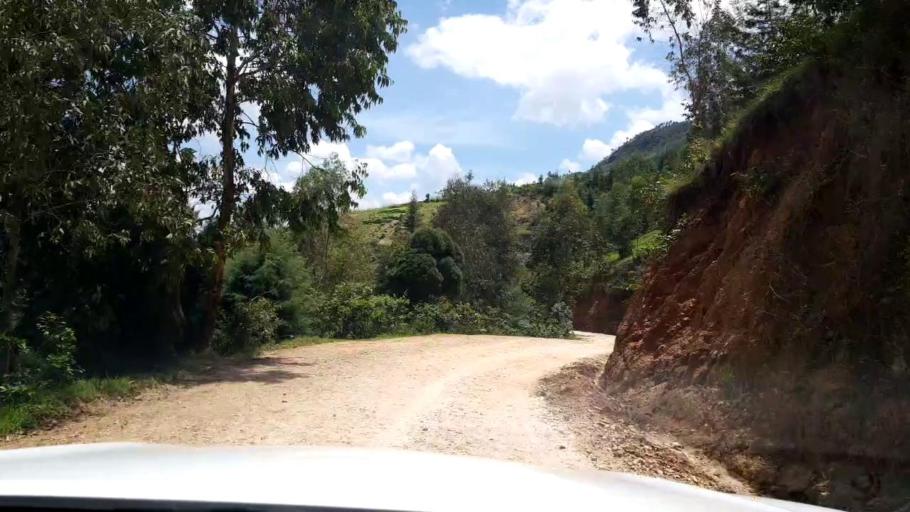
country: RW
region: Southern Province
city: Gitarama
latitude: -1.9828
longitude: 29.6197
